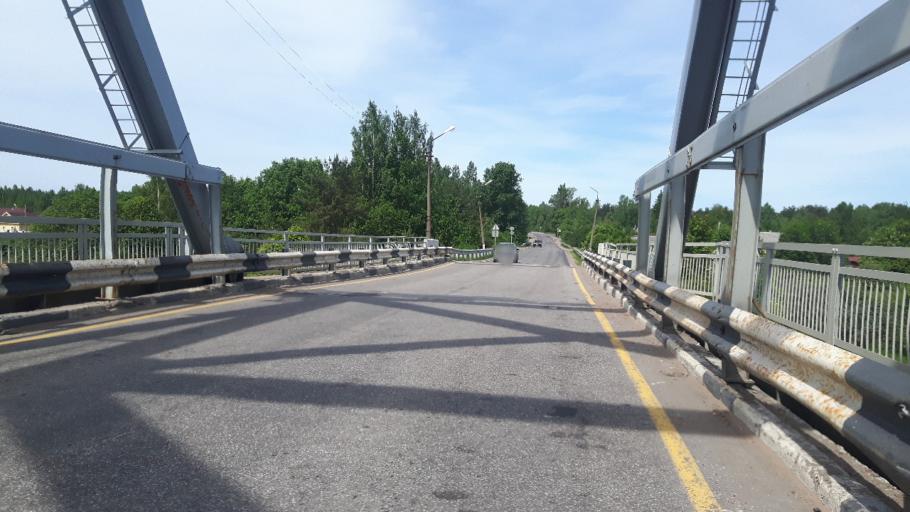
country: RU
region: Leningrad
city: Ust'-Luga
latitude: 59.6535
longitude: 28.2573
